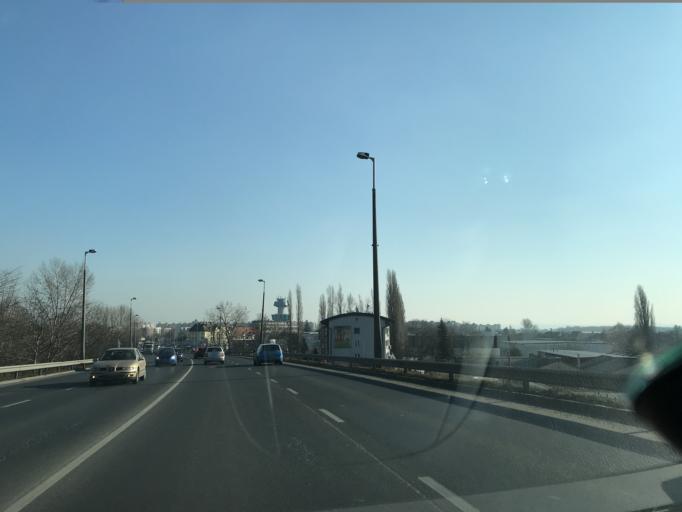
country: HU
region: Gyor-Moson-Sopron
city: Gyor
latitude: 47.6777
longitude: 17.6262
